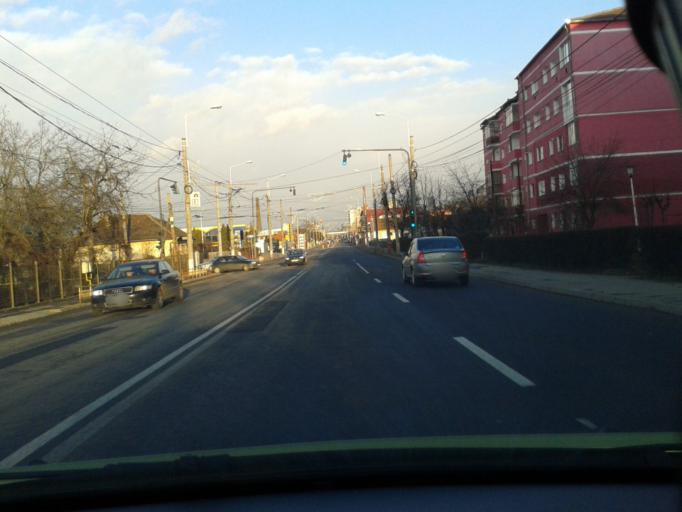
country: RO
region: Sibiu
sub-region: Municipiul Medias
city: Medias
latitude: 46.1512
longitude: 24.3312
